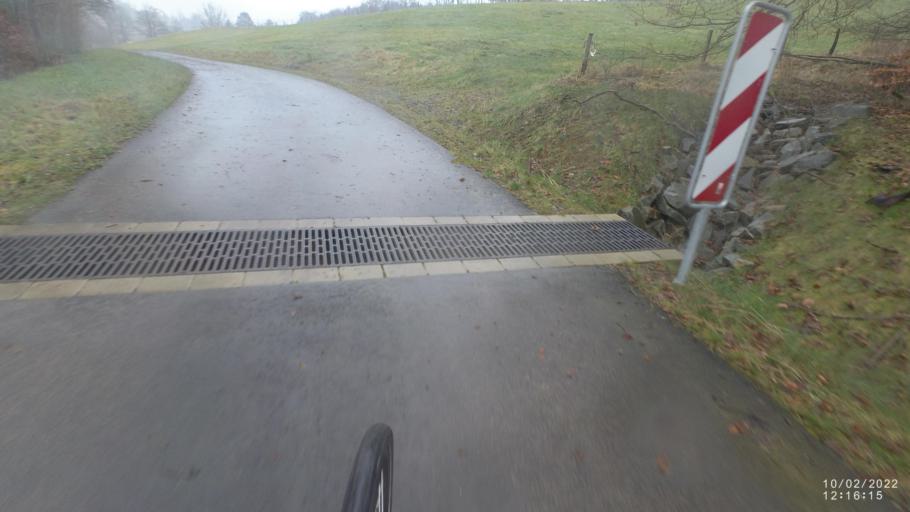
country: DE
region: North Rhine-Westphalia
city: Kierspe
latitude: 51.1475
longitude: 7.6112
